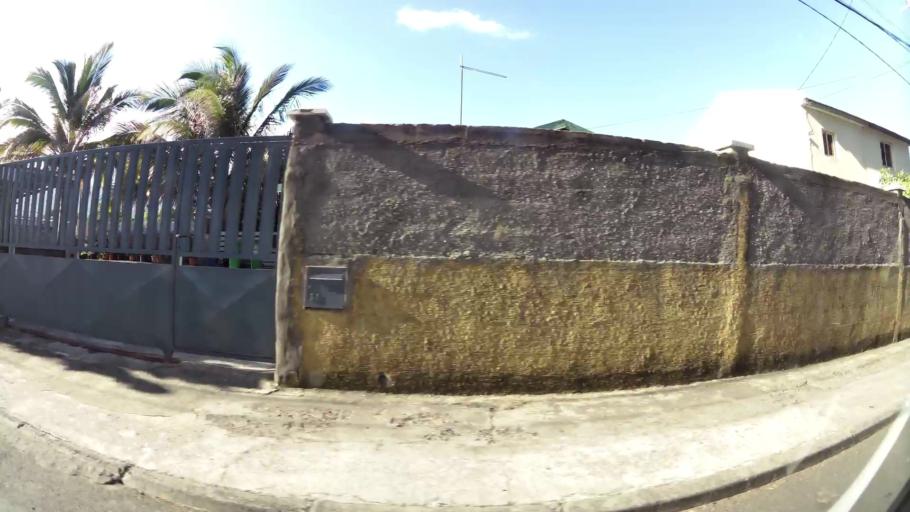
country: RE
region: Reunion
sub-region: Reunion
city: Saint-Louis
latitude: -21.2959
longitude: 55.3977
